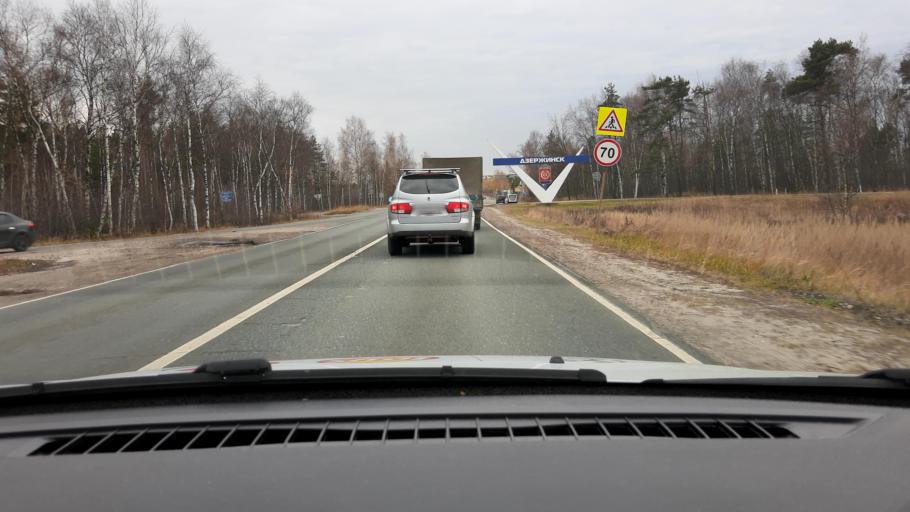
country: RU
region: Nizjnij Novgorod
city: Dzerzhinsk
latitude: 56.2973
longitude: 43.4765
